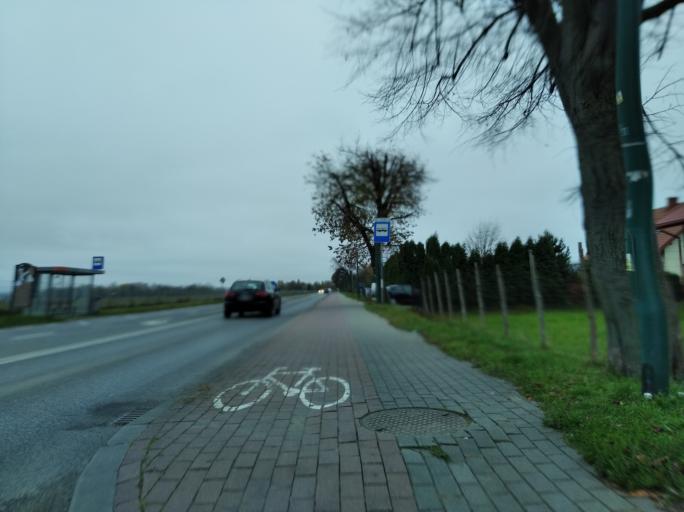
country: PL
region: Subcarpathian Voivodeship
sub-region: Krosno
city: Krosno
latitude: 49.6869
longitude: 21.7244
